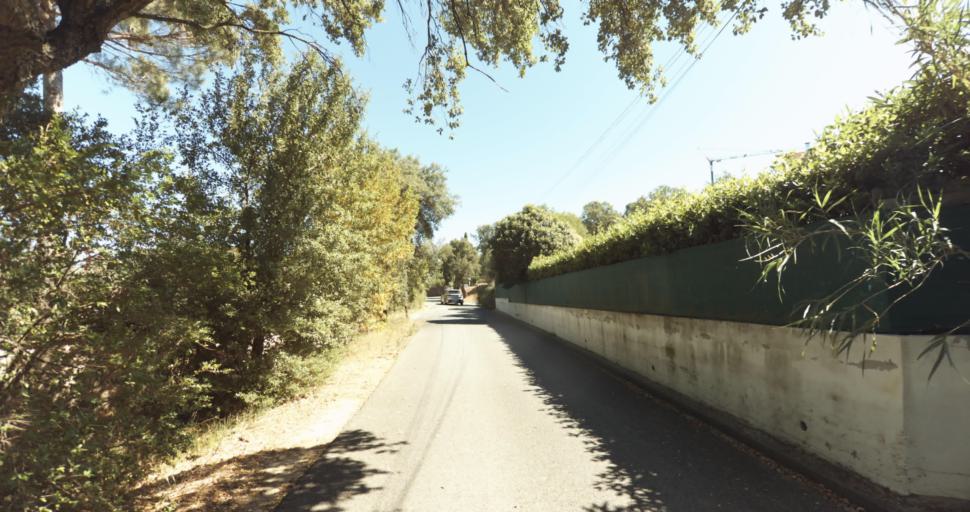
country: FR
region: Provence-Alpes-Cote d'Azur
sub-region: Departement du Var
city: Gassin
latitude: 43.2564
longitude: 6.6001
